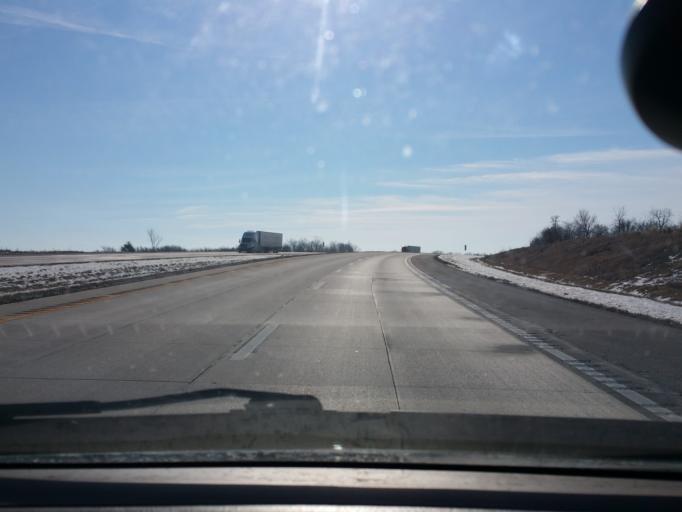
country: US
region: Missouri
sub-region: Daviess County
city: Gallatin
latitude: 39.9767
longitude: -94.0944
